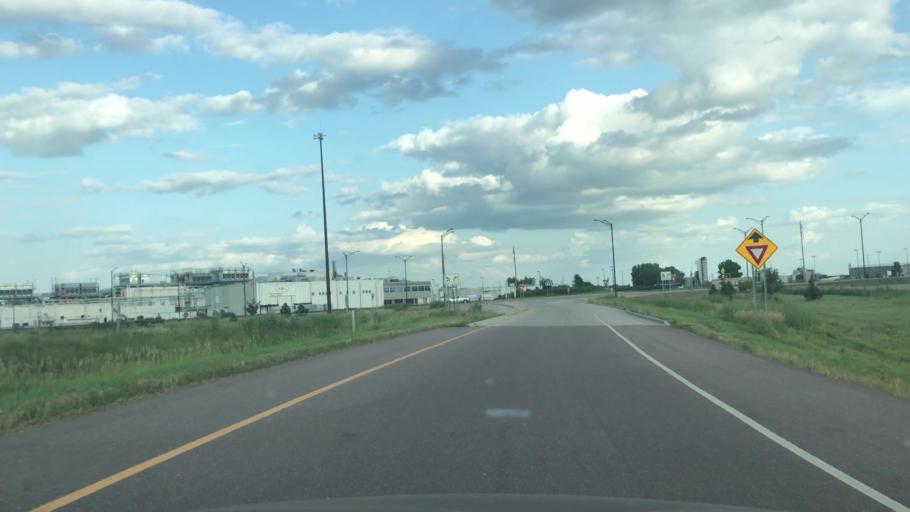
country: US
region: Minnesota
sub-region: Nobles County
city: Worthington
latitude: 43.6367
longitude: -95.5703
